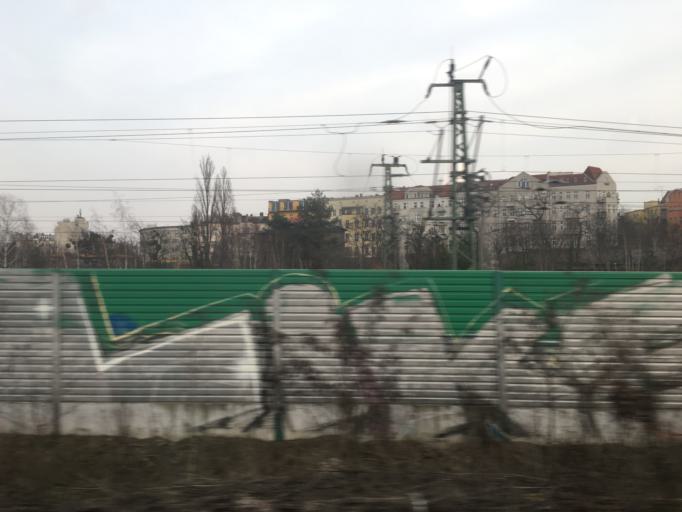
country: DE
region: Berlin
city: Berlin Schoeneberg
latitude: 52.4887
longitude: 13.3718
